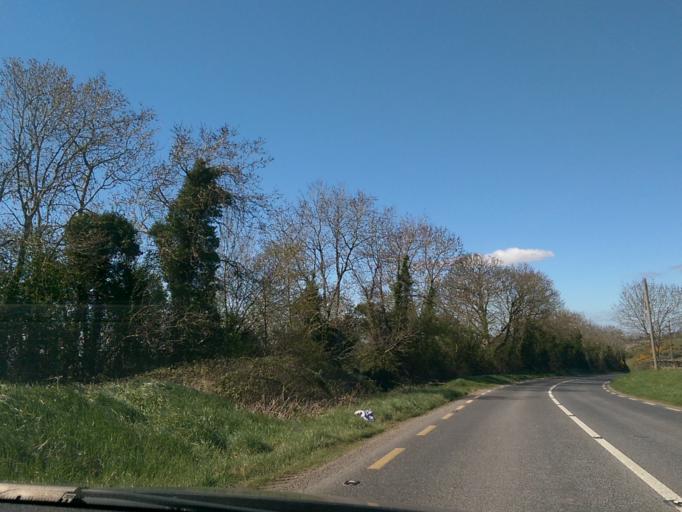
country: IE
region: Leinster
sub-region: Kildare
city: Moone
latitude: 52.9846
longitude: -6.7835
